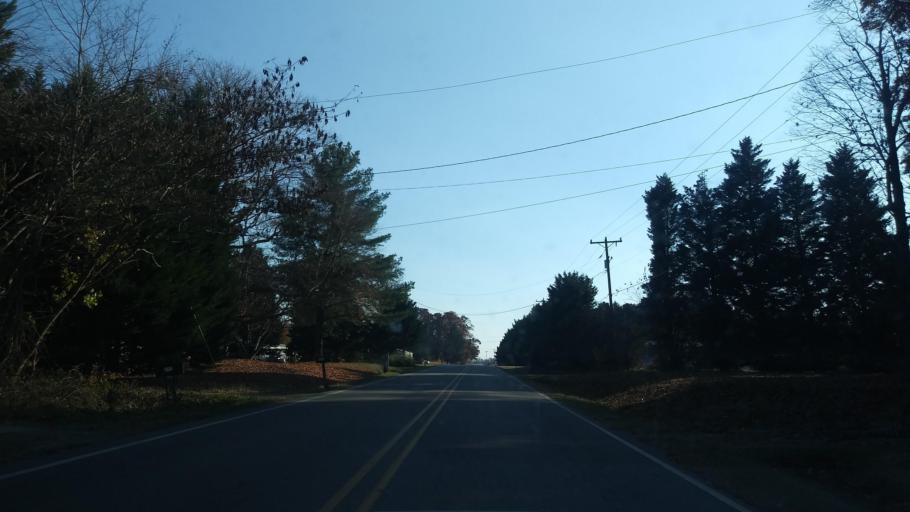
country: US
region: North Carolina
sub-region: Rockingham County
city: Reidsville
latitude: 36.2552
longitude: -79.7228
